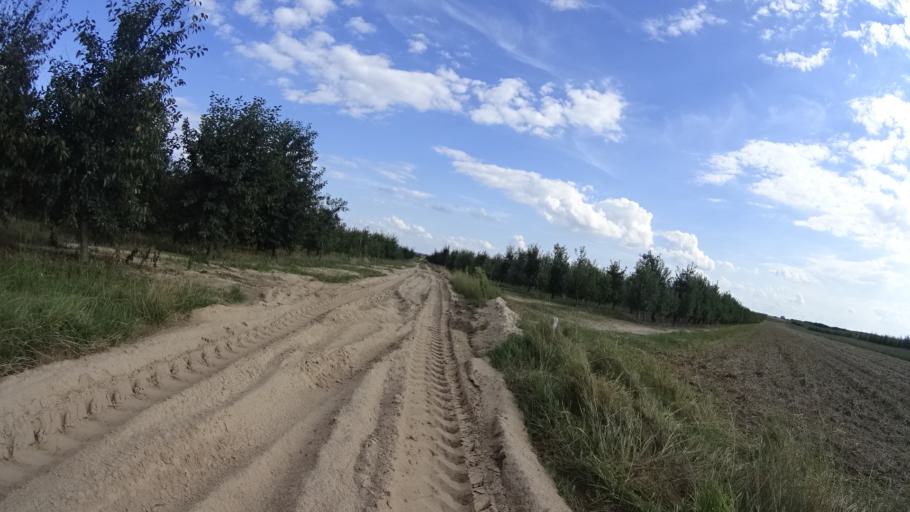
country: PL
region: Masovian Voivodeship
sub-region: Powiat bialobrzeski
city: Wysmierzyce
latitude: 51.6663
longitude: 20.8115
